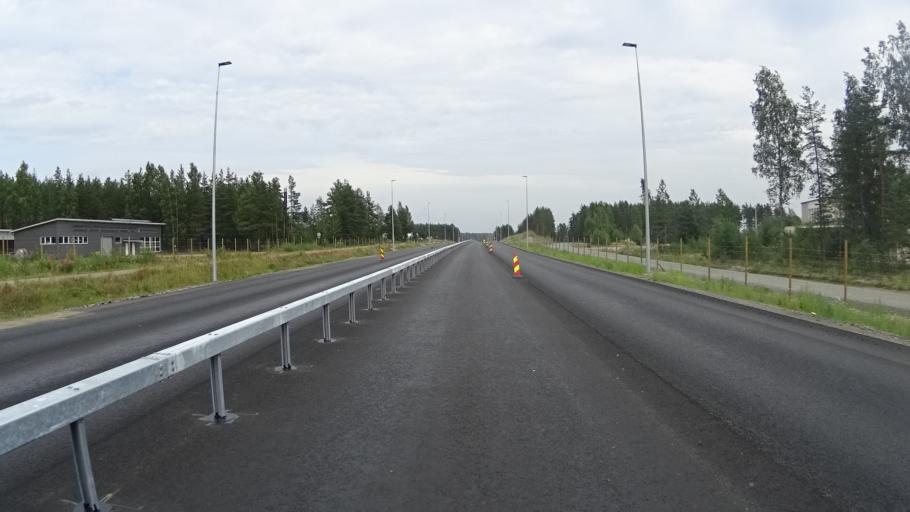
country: FI
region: South Karelia
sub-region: Lappeenranta
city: Luumaeki
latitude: 60.9321
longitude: 27.6510
